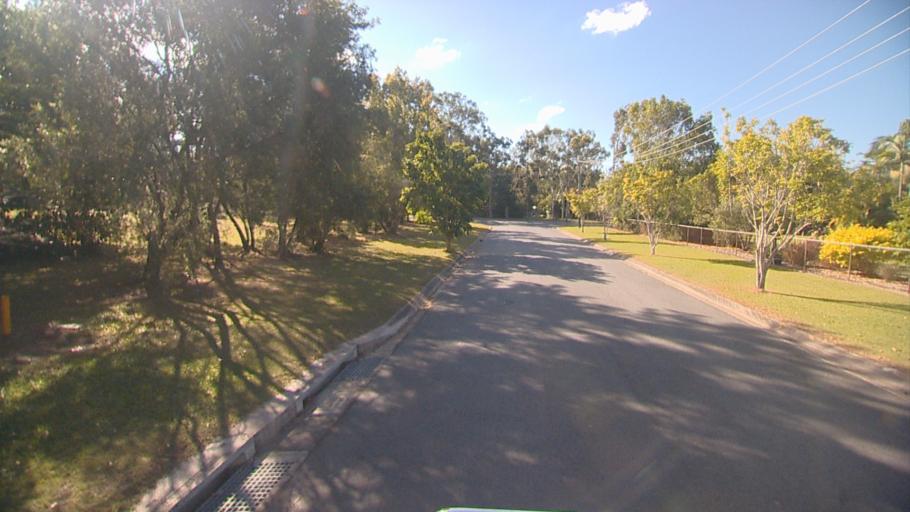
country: AU
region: Queensland
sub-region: Logan
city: Park Ridge South
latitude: -27.7060
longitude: 153.0152
